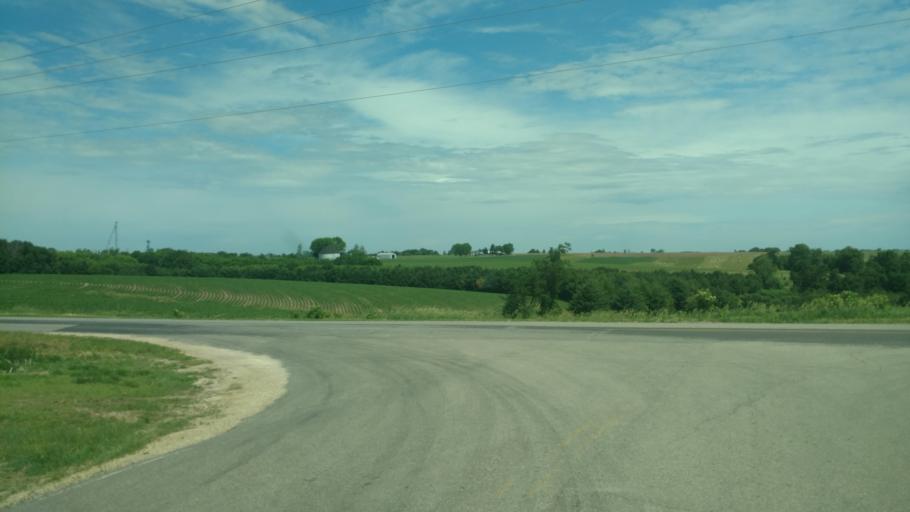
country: US
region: Wisconsin
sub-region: Vernon County
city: Hillsboro
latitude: 43.6994
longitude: -90.4478
